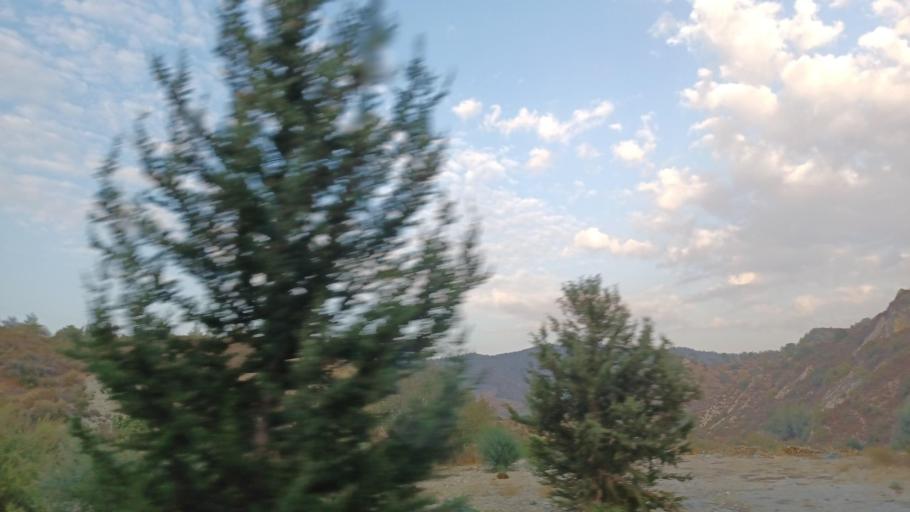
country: CY
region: Limassol
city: Pelendri
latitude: 34.8130
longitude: 32.9590
